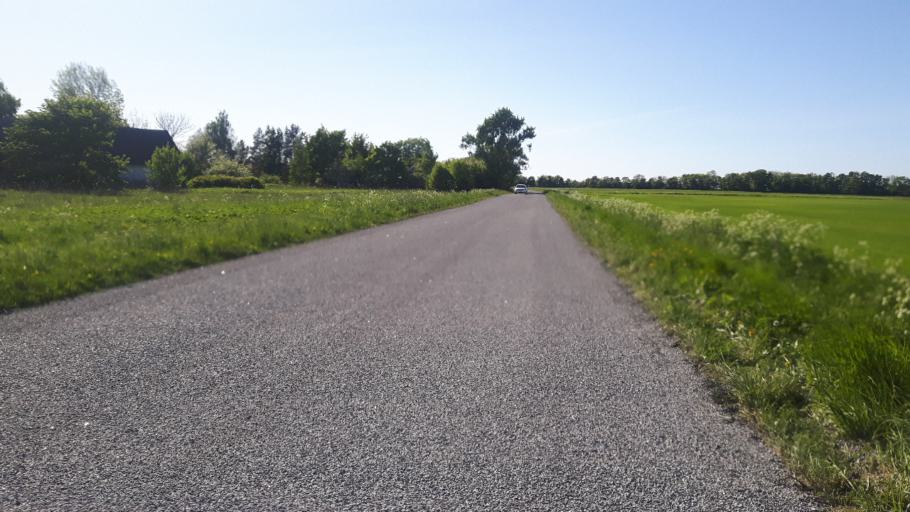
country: EE
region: Ida-Virumaa
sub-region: Kohtla-Jaerve linn
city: Kohtla-Jarve
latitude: 59.4365
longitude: 27.1994
